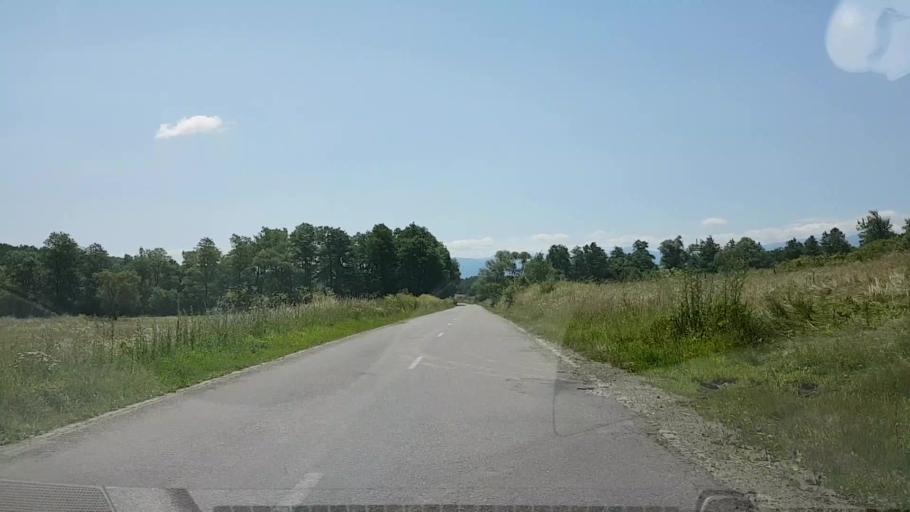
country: RO
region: Brasov
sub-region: Comuna Cincu
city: Cincu
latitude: 45.8808
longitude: 24.8140
